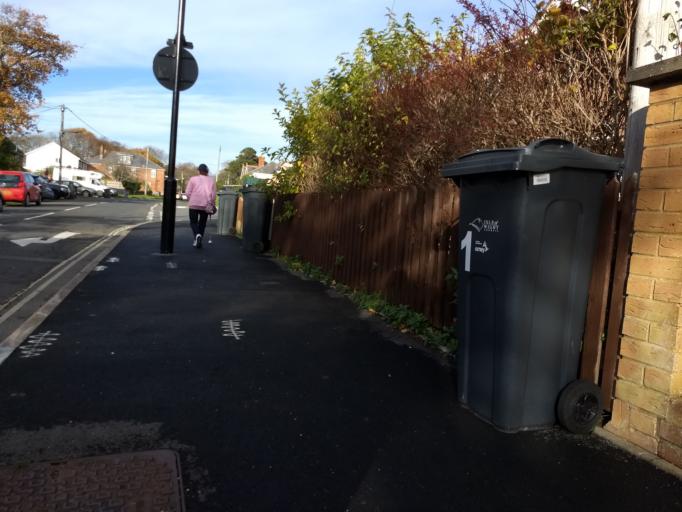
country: GB
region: England
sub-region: Isle of Wight
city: Totland
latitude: 50.6861
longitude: -1.5271
